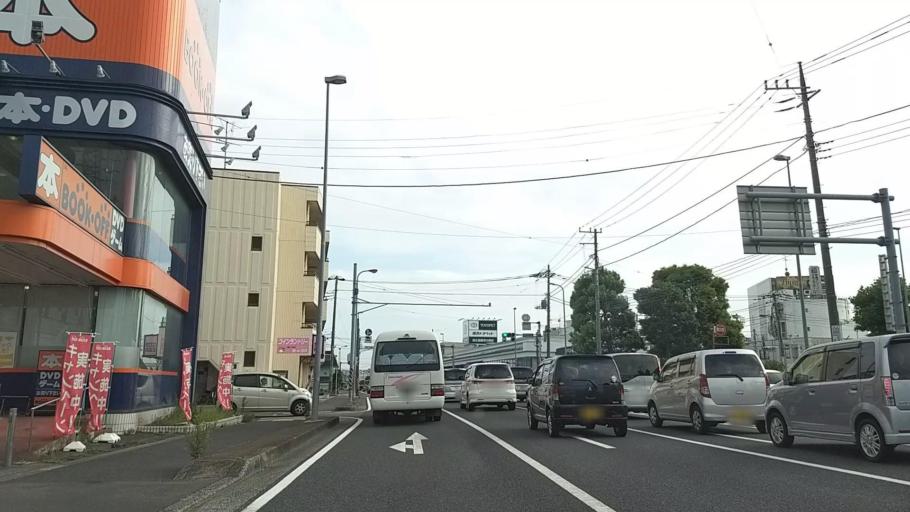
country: JP
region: Kanagawa
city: Hiratsuka
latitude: 35.3524
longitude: 139.3566
